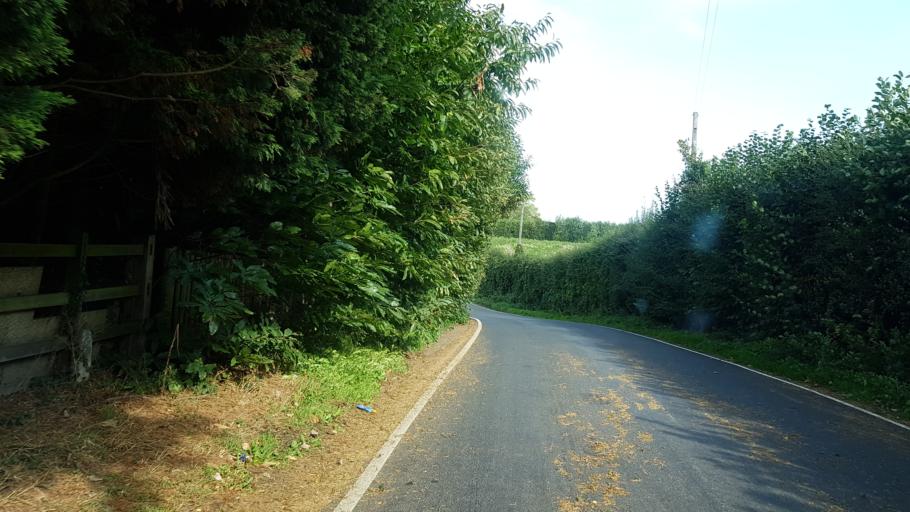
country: GB
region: England
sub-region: Kent
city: Yalding
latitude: 51.2394
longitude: 0.4659
